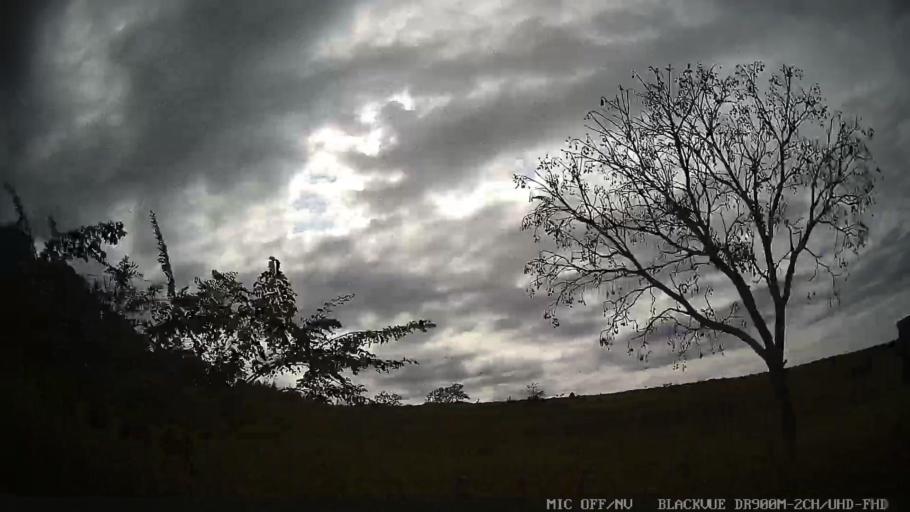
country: BR
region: Sao Paulo
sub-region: Itupeva
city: Itupeva
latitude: -23.1667
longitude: -47.1305
